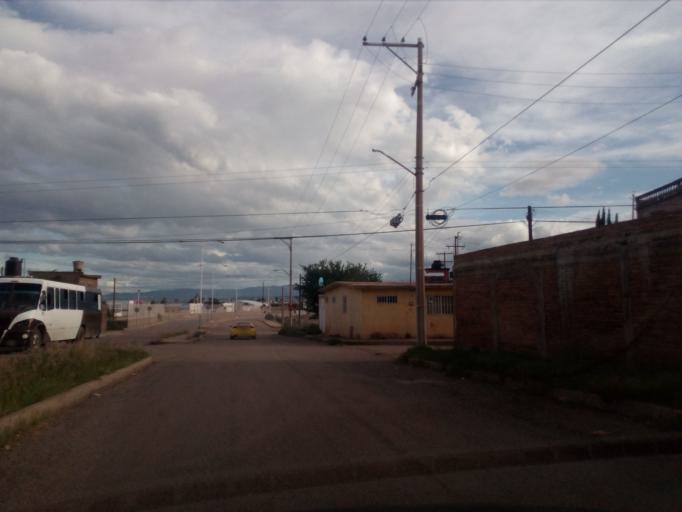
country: MX
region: Durango
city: Victoria de Durango
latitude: 24.0493
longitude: -104.6638
